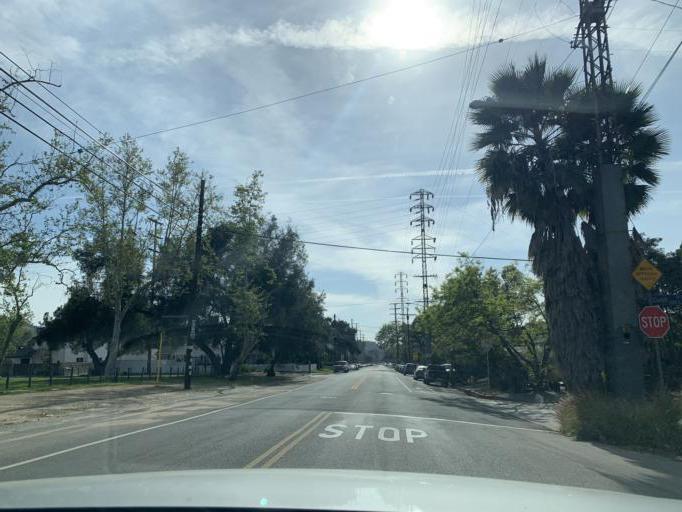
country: US
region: California
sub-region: Los Angeles County
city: South Pasadena
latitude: 34.1201
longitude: -118.1699
